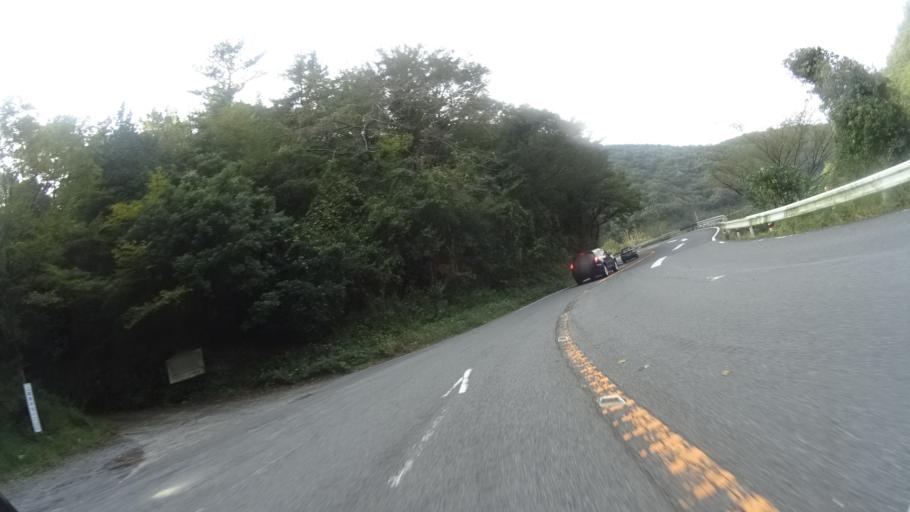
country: JP
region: Oita
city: Beppu
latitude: 33.2791
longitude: 131.4526
